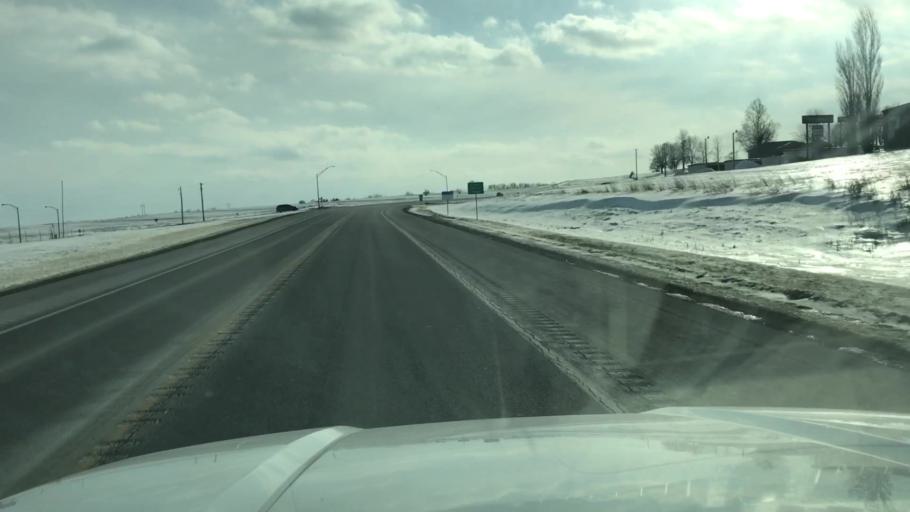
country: US
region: Missouri
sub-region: Nodaway County
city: Maryville
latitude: 40.3362
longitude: -94.8539
